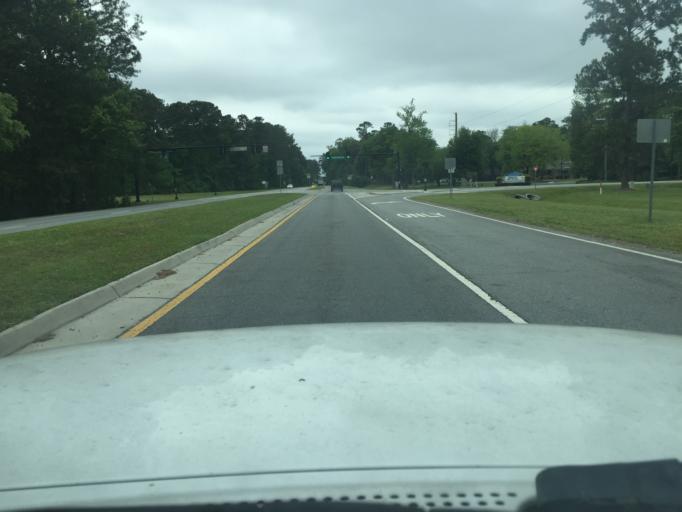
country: US
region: Georgia
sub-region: Chatham County
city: Skidaway Island
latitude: 31.9399
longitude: -81.0560
